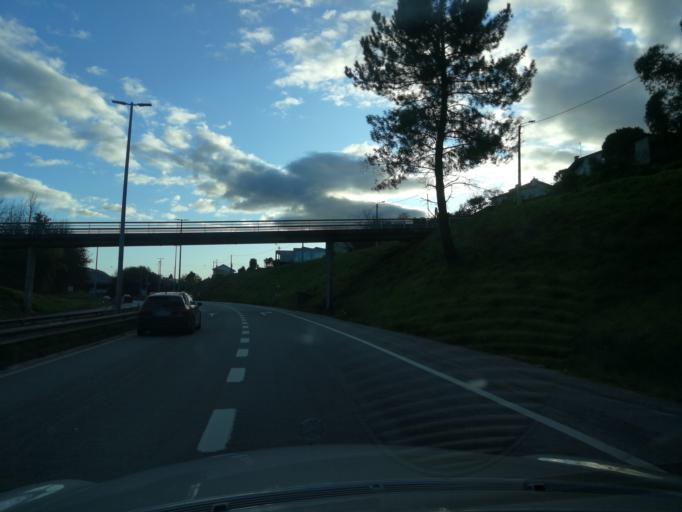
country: PT
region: Braga
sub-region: Barcelos
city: Vila Frescainha
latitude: 41.5338
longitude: -8.6394
